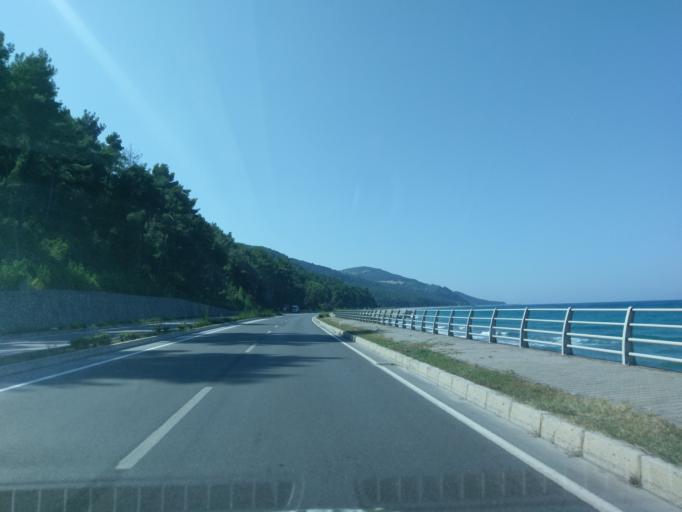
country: TR
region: Samsun
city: Yakakent
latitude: 41.6460
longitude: 35.4725
